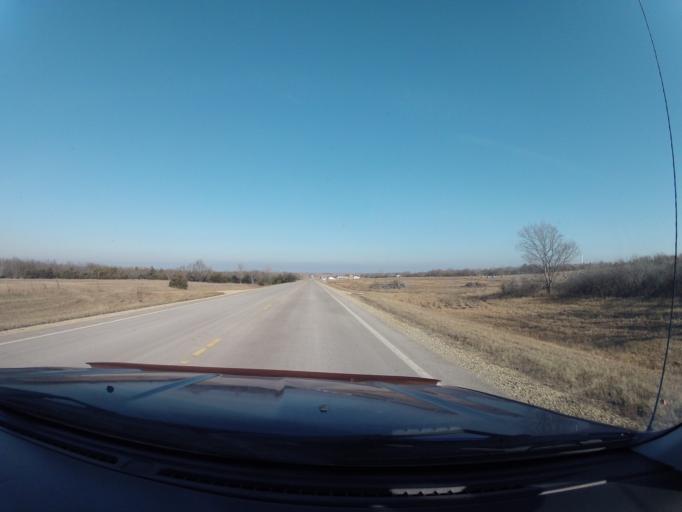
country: US
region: Kansas
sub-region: Marshall County
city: Blue Rapids
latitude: 39.4235
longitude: -96.7644
